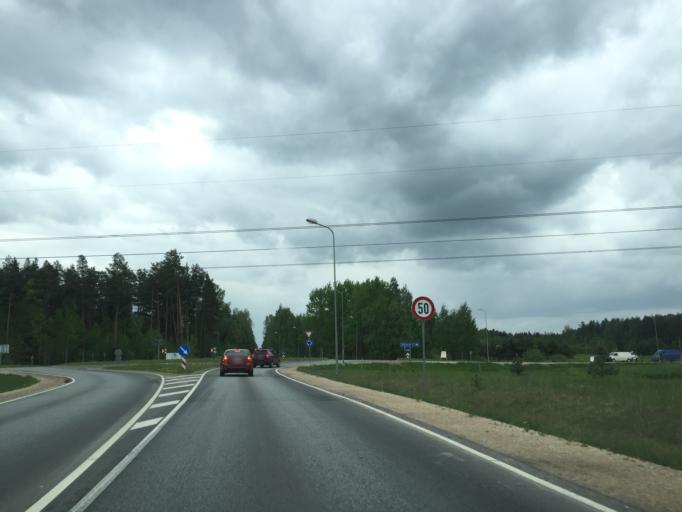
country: LV
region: Ogre
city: Ogre
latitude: 56.8596
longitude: 24.5641
